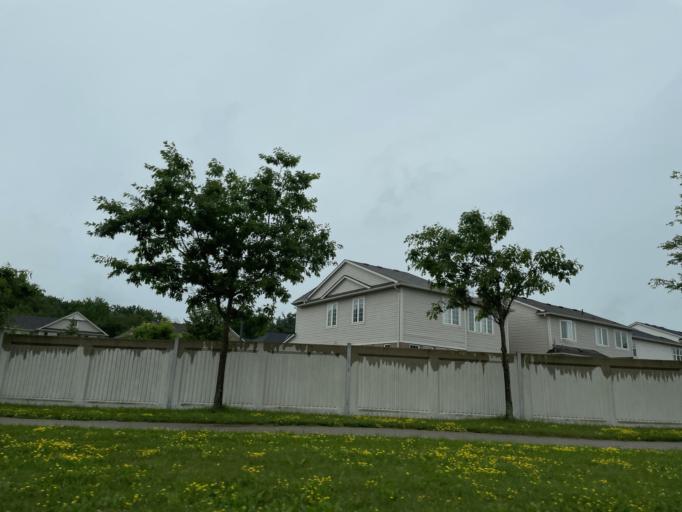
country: CA
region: Ontario
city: Cambridge
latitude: 43.4010
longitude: -80.2921
